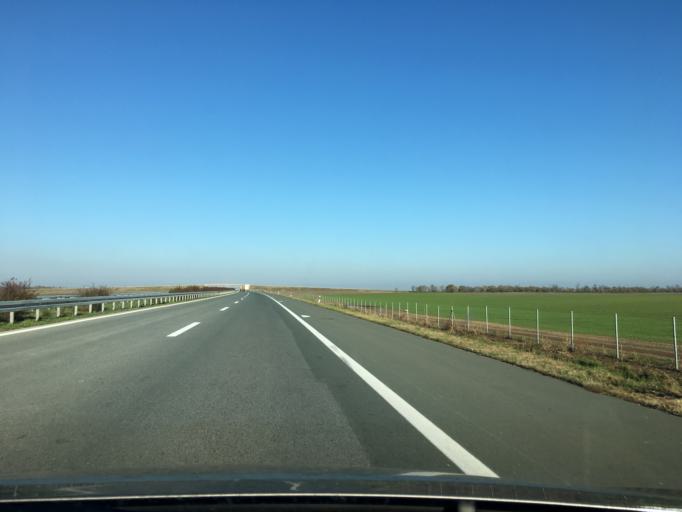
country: RS
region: Autonomna Pokrajina Vojvodina
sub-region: Severnobacki Okrug
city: Mali Igos
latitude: 45.6904
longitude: 19.7257
